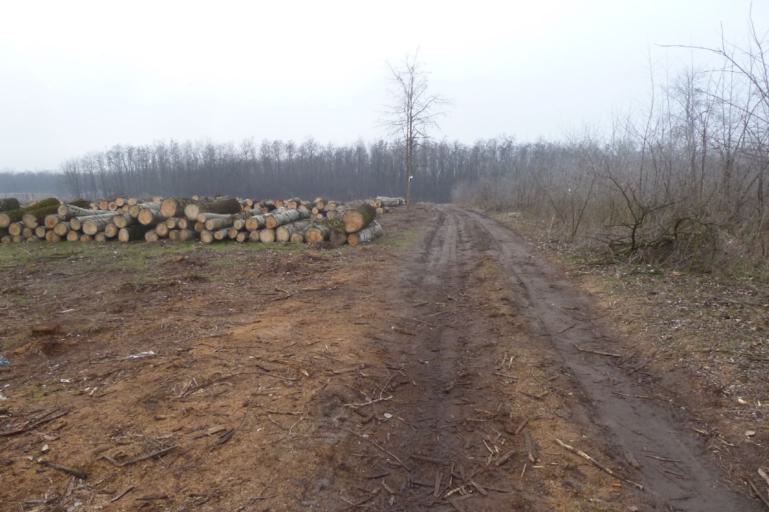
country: HU
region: Pest
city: Tapiosag
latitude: 47.4109
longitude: 19.6352
